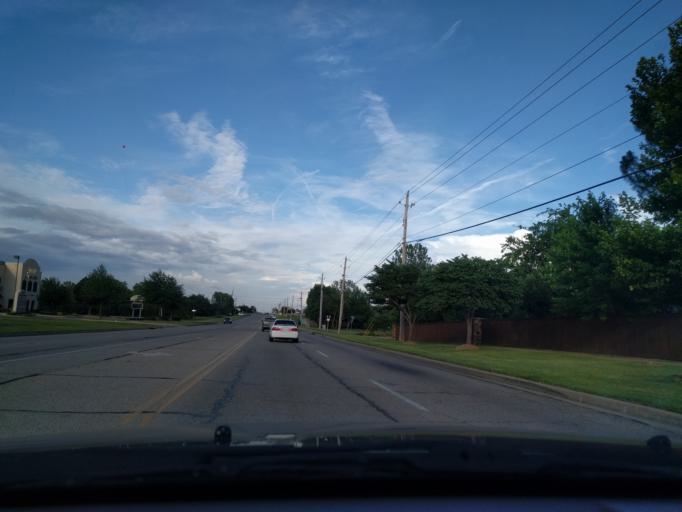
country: US
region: Oklahoma
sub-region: Tulsa County
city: Broken Arrow
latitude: 36.0609
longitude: -95.8250
